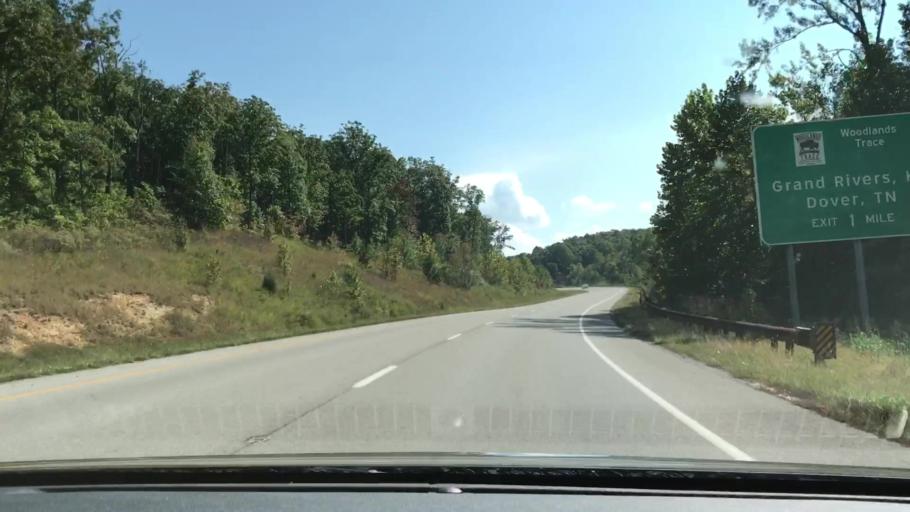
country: US
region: Kentucky
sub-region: Trigg County
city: Cadiz
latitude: 36.7788
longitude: -88.0900
